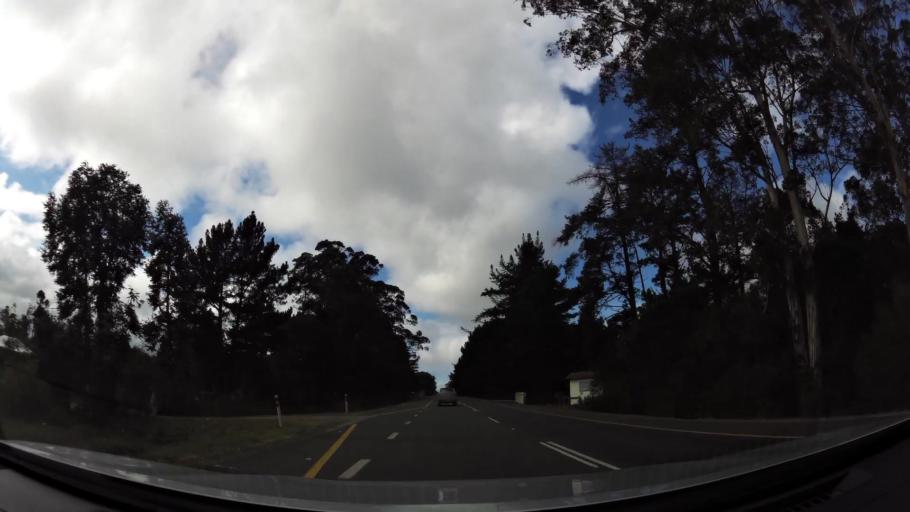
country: ZA
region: Western Cape
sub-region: Eden District Municipality
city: Plettenberg Bay
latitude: -34.0443
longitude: 23.2888
